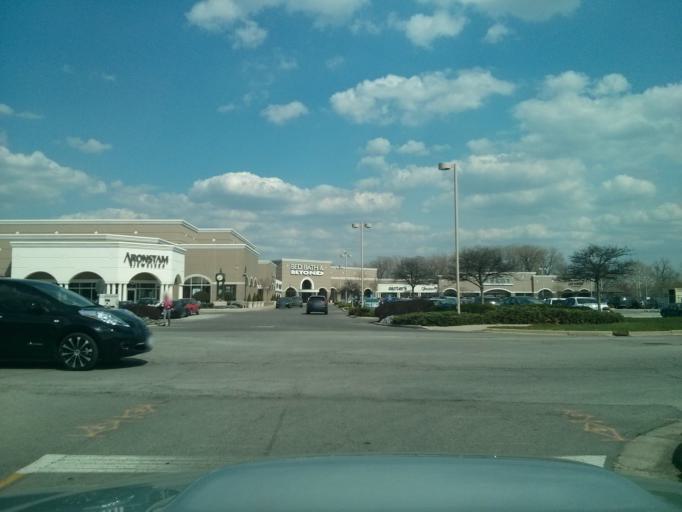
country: US
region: Indiana
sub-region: Marion County
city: Meridian Hills
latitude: 39.9134
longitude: -86.1069
